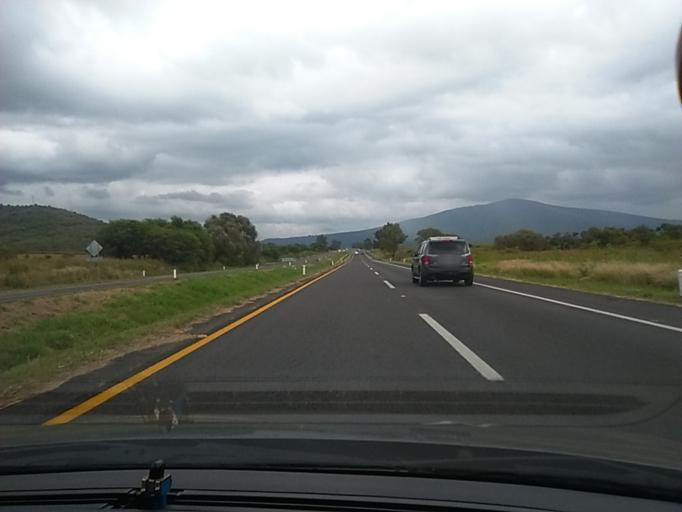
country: MX
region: Jalisco
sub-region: Zapotlanejo
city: La Mezquitera
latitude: 20.5773
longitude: -103.0900
